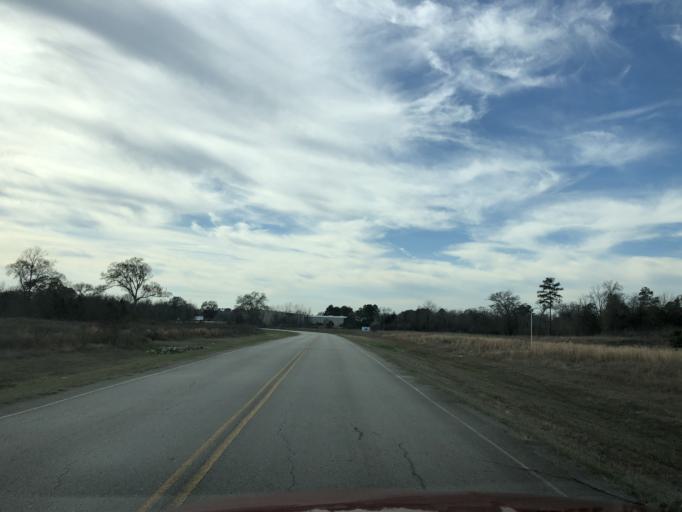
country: US
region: Texas
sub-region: Montgomery County
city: Magnolia
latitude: 30.4018
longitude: -95.6942
